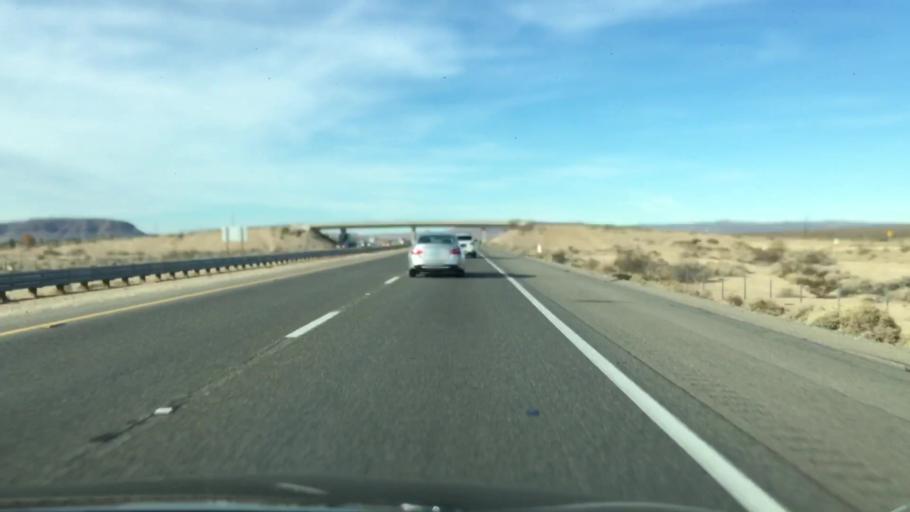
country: US
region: California
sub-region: San Bernardino County
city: Barstow
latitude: 34.9111
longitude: -116.8178
